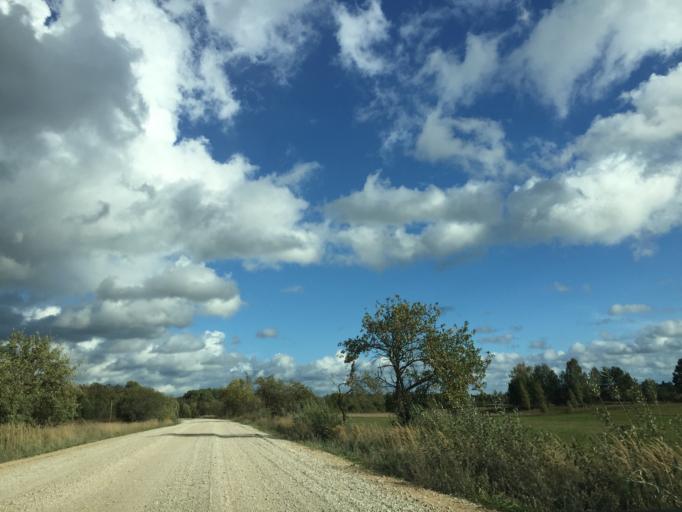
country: LV
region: Malpils
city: Malpils
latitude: 57.0150
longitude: 25.0013
